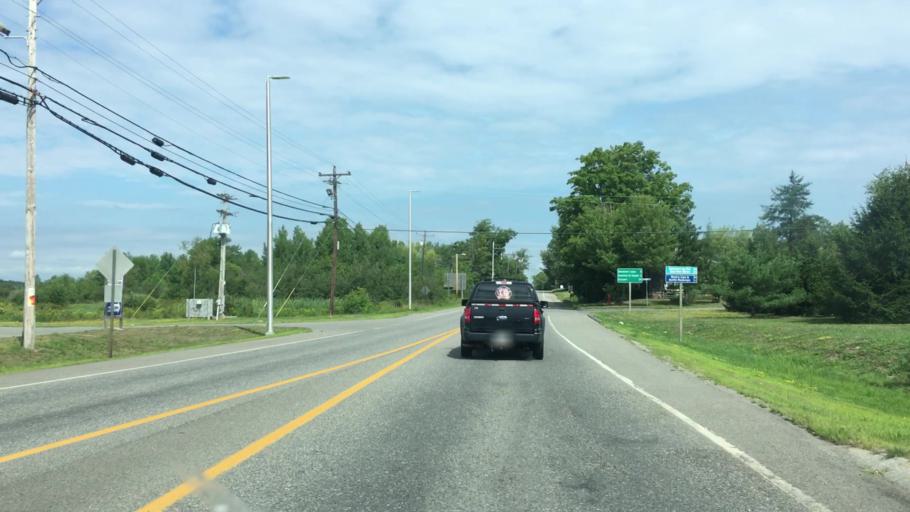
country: US
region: Maine
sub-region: Washington County
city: Calais
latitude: 45.1619
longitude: -67.2911
